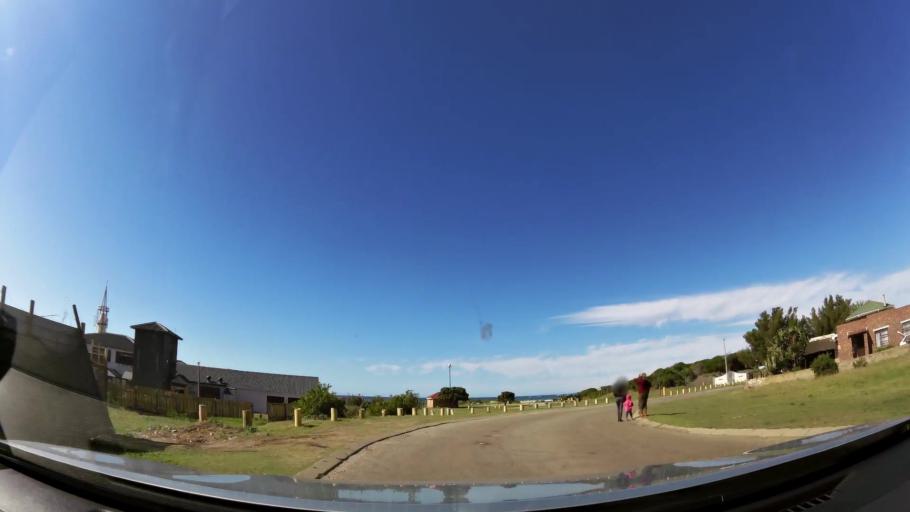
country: ZA
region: Eastern Cape
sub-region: Cacadu District Municipality
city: Jeffrey's Bay
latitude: -34.0578
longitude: 24.9228
